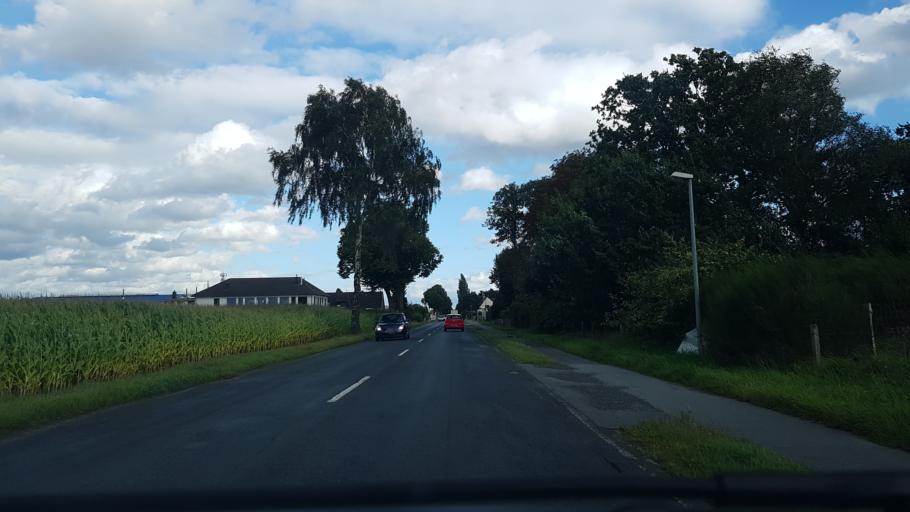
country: DE
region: Lower Saxony
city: Achim
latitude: 53.0215
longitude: 8.9950
